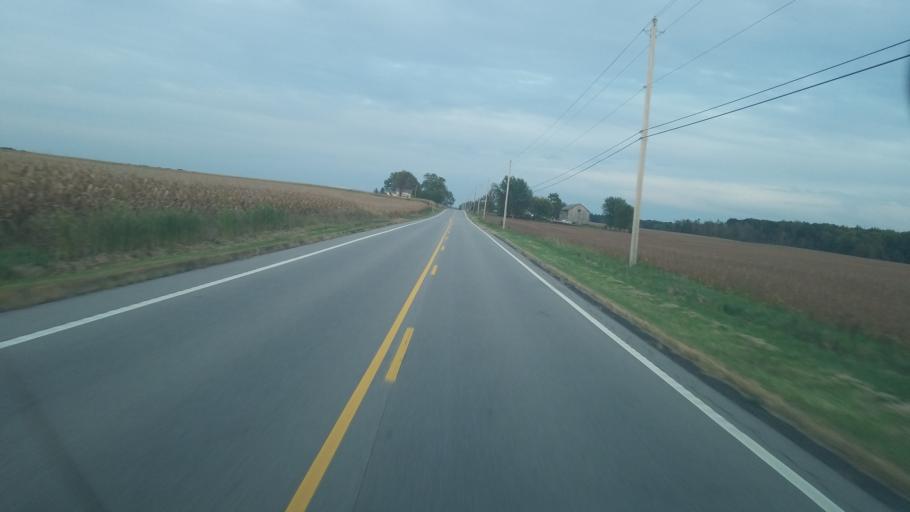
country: US
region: Ohio
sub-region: Ashtabula County
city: Roaming Shores
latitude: 41.6069
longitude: -80.7010
